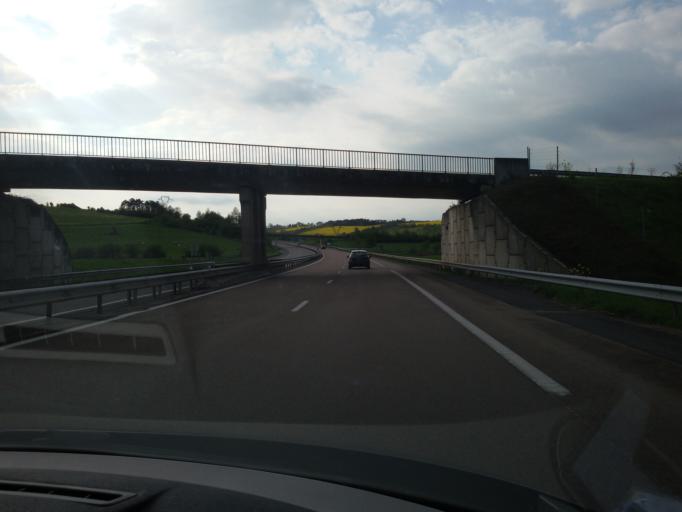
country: FR
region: Champagne-Ardenne
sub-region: Departement de la Haute-Marne
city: Chateauvillain
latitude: 48.0751
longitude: 4.8896
